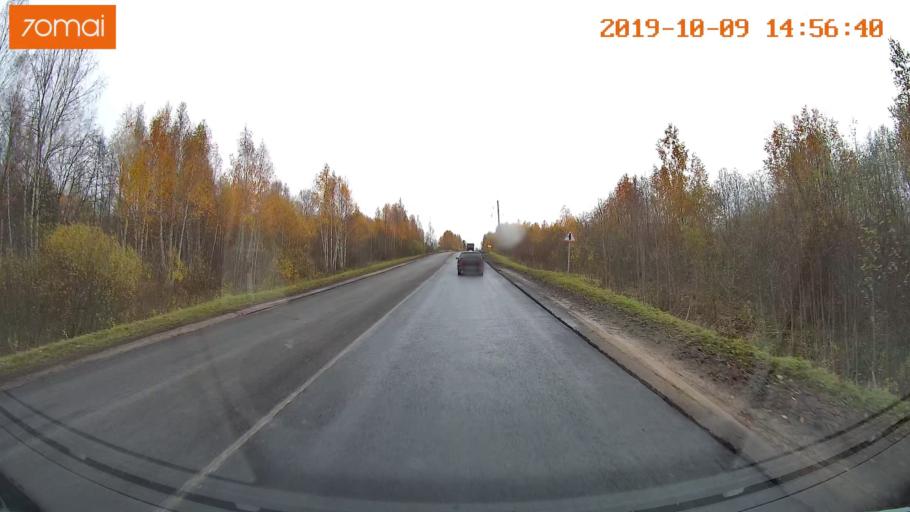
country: RU
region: Kostroma
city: Chistyye Bory
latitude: 58.3441
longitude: 41.6481
